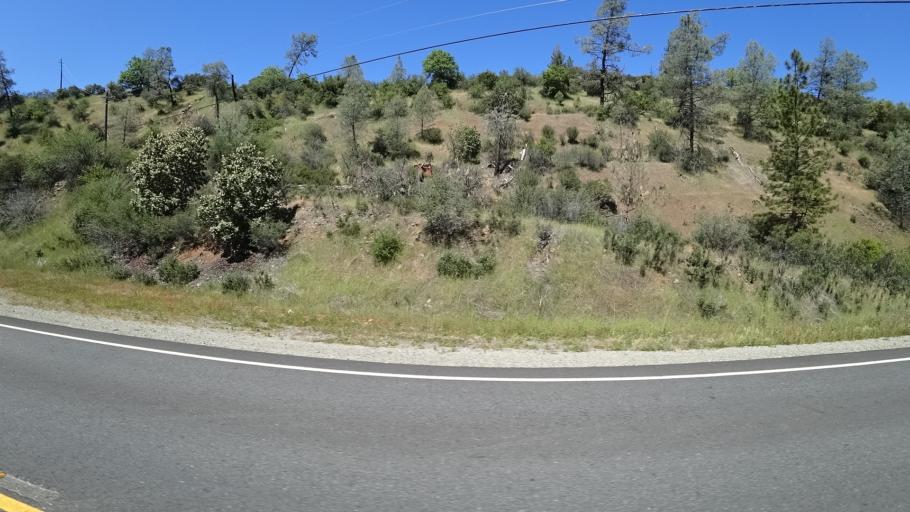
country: US
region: California
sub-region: Trinity County
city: Weaverville
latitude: 40.7252
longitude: -123.0501
